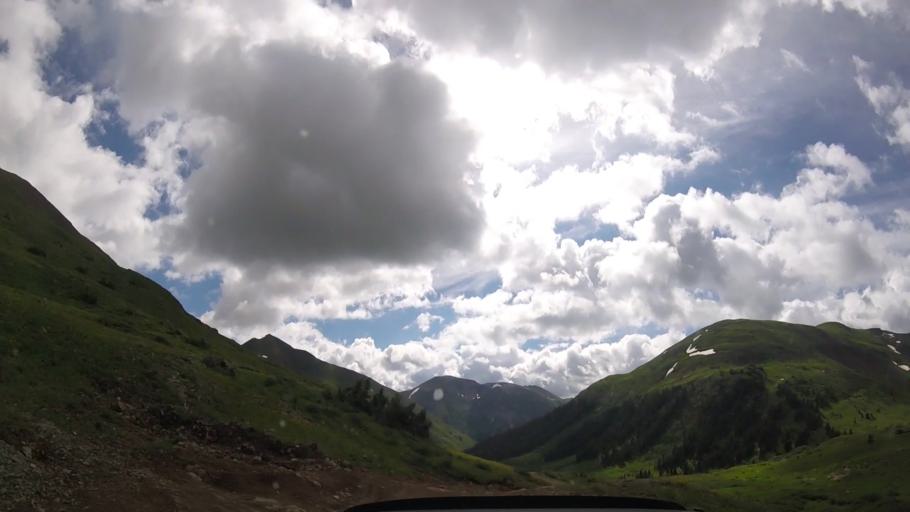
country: US
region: Colorado
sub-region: Ouray County
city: Ouray
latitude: 37.9324
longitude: -107.5924
